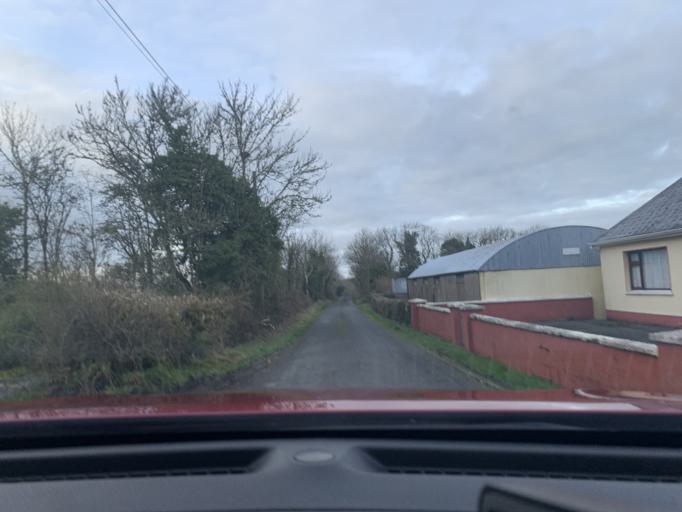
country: IE
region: Connaught
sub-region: Sligo
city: Ballymote
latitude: 54.0049
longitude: -8.5747
